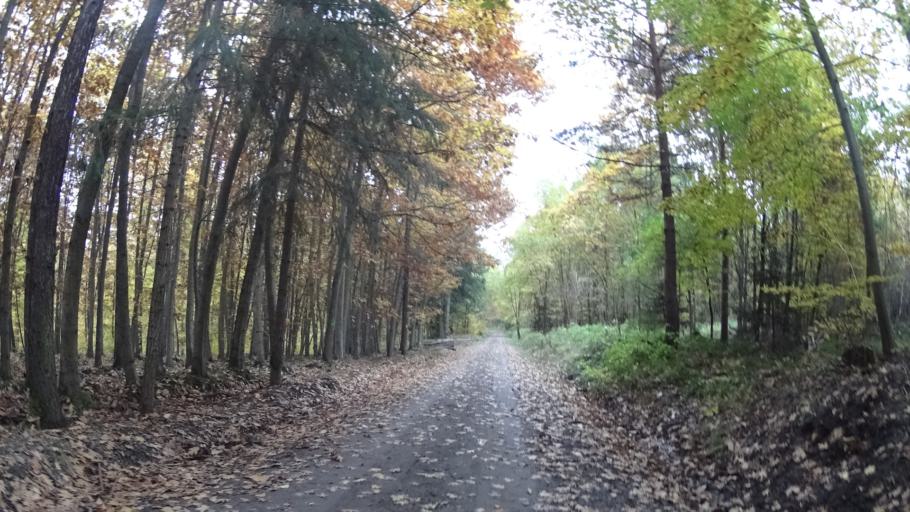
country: DE
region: Thuringia
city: Freienorla
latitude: 50.7608
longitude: 11.5725
